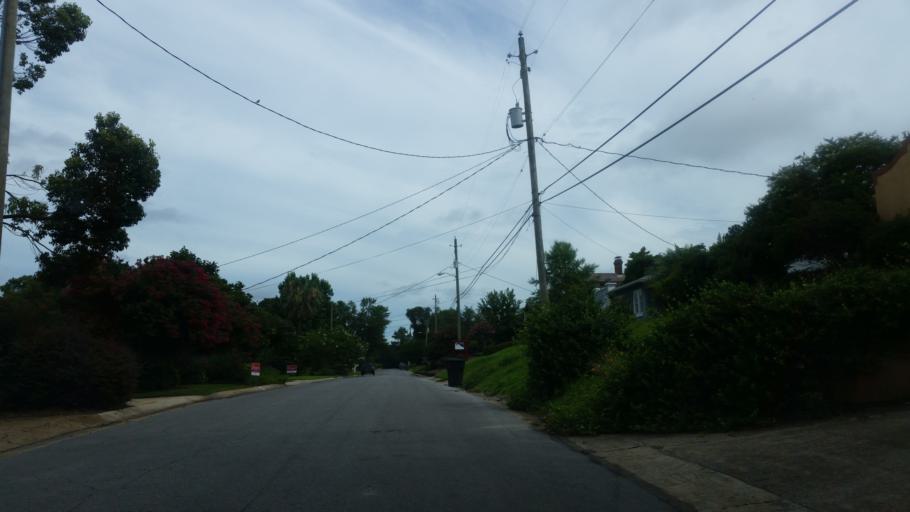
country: US
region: Florida
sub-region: Escambia County
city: East Pensacola Heights
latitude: 30.4366
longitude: -87.1898
